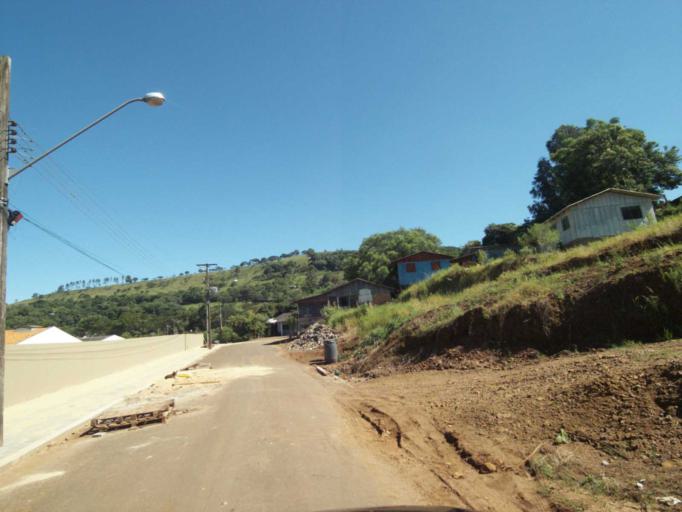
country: BR
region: Parana
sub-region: Francisco Beltrao
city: Francisco Beltrao
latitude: -26.1449
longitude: -53.3064
